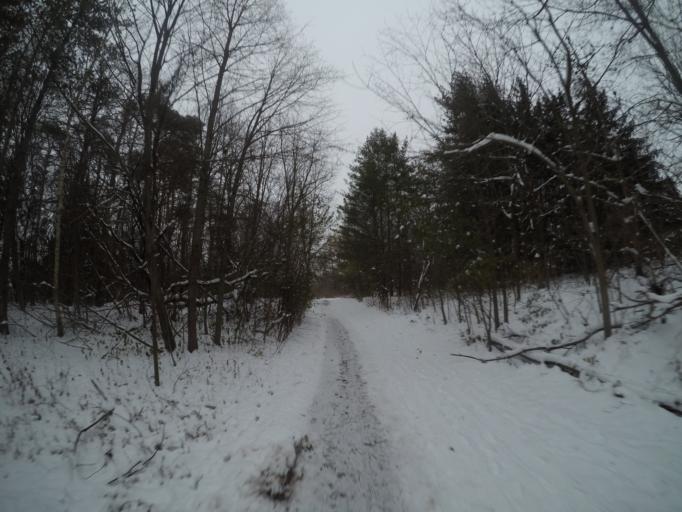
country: CA
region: Ontario
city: Waterloo
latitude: 43.4862
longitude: -80.5065
